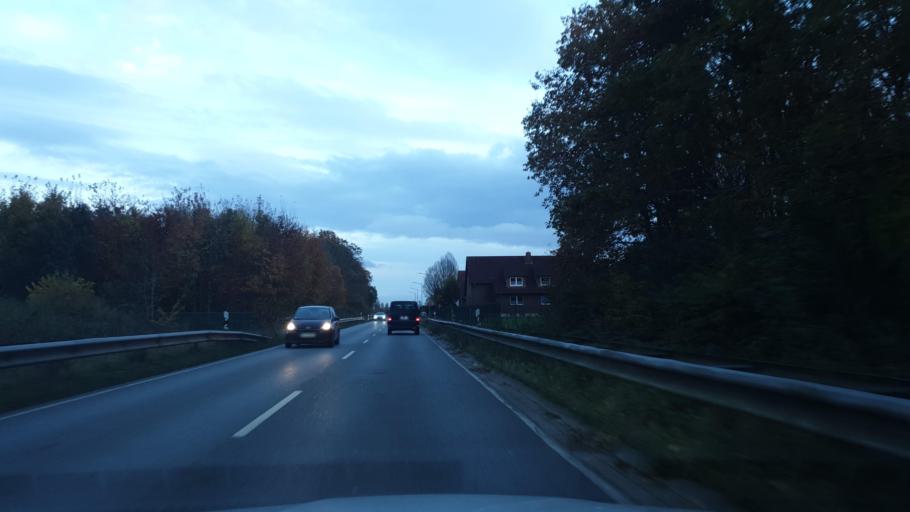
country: DE
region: North Rhine-Westphalia
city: Buende
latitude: 52.1935
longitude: 8.5439
